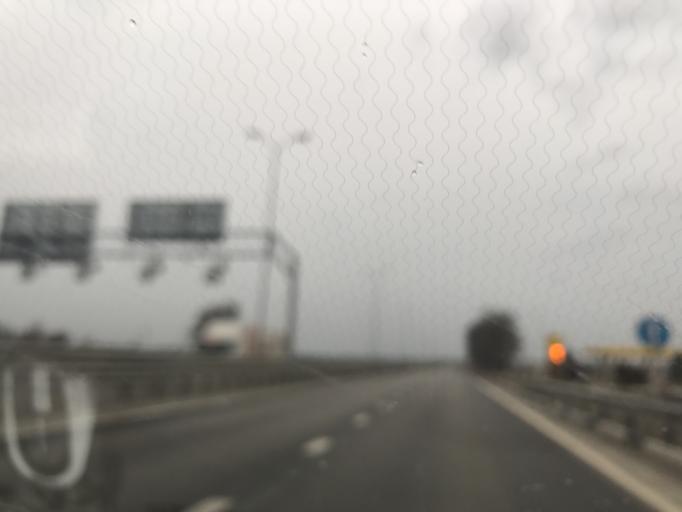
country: RU
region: Krasnodarskiy
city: Pavlovskaya
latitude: 46.1270
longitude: 39.8623
